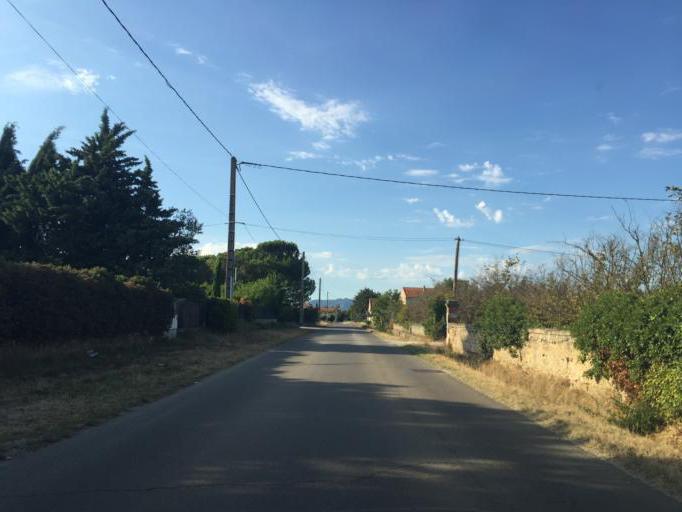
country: FR
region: Provence-Alpes-Cote d'Azur
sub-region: Departement du Vaucluse
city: Pernes-les-Fontaines
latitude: 44.0224
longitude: 5.0538
